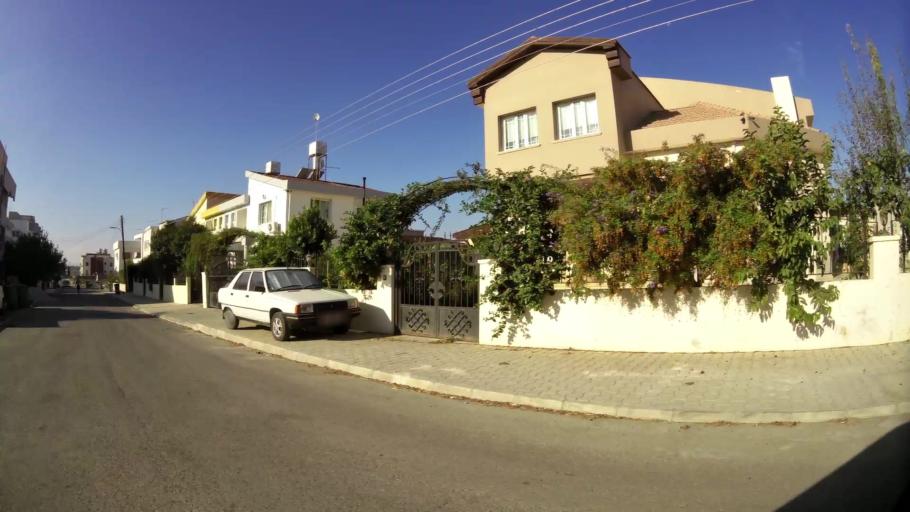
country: CY
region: Lefkosia
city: Nicosia
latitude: 35.2141
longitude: 33.2935
